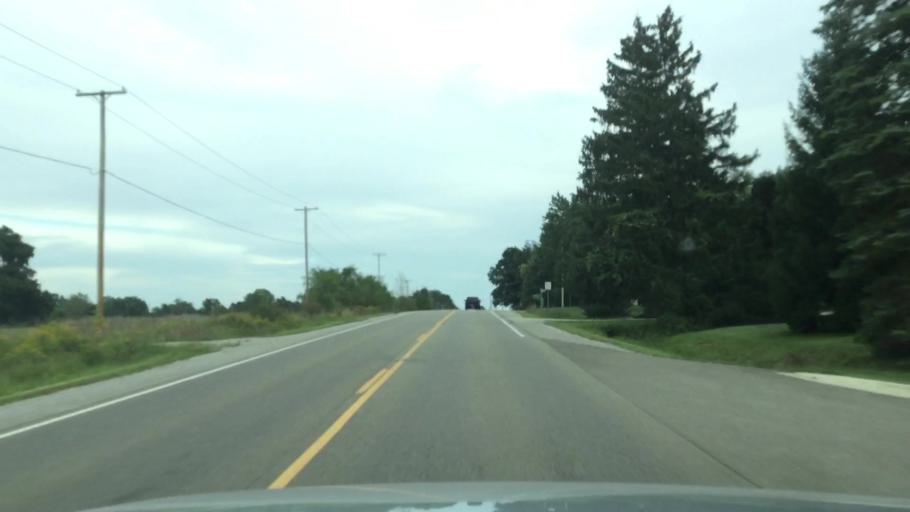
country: US
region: Michigan
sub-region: Genesee County
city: Lake Fenton
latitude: 42.8858
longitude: -83.6872
